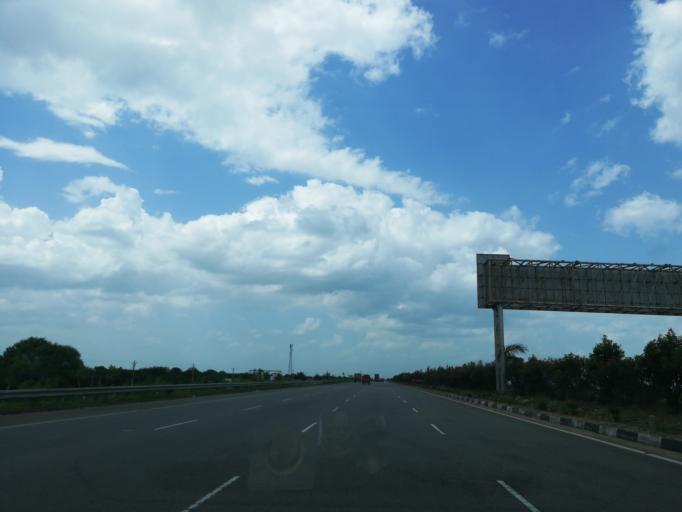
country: IN
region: Telangana
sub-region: Medak
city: Patancheru
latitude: 17.4838
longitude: 78.2462
